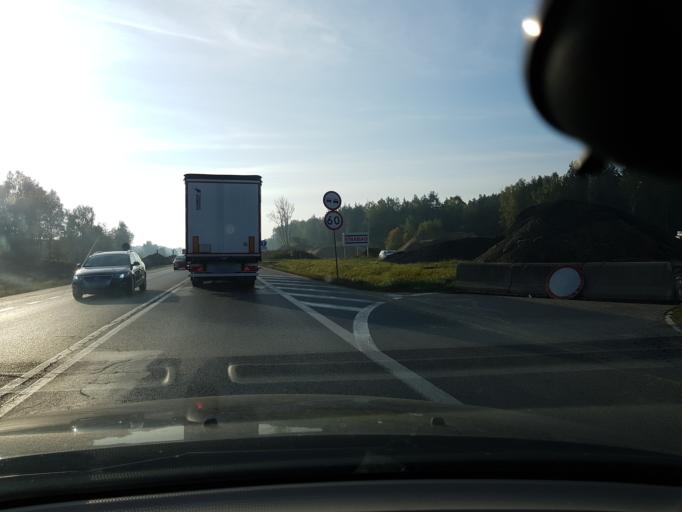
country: PL
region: Masovian Voivodeship
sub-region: Powiat otwocki
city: Otwock
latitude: 52.1630
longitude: 21.3008
